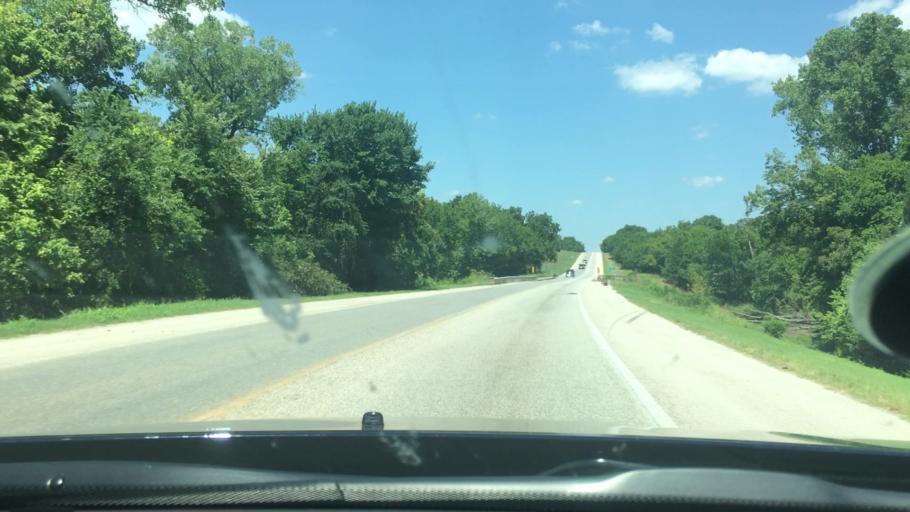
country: US
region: Oklahoma
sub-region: Marshall County
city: Oakland
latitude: 34.1748
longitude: -96.8568
